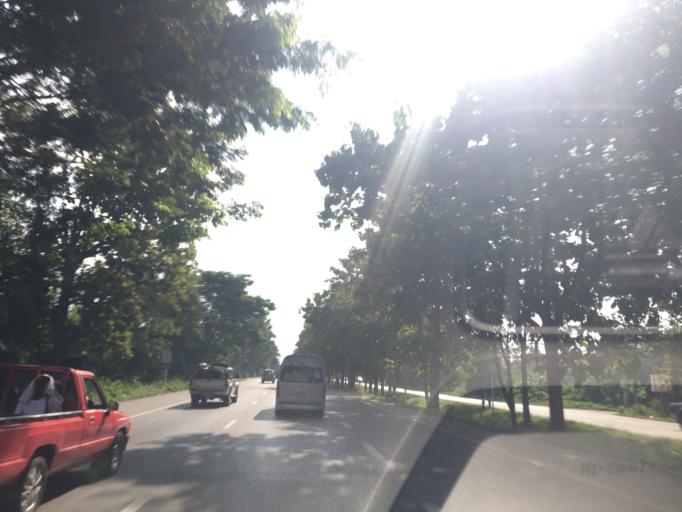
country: TH
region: Chiang Rai
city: Mae Lao
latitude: 19.7454
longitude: 99.7261
